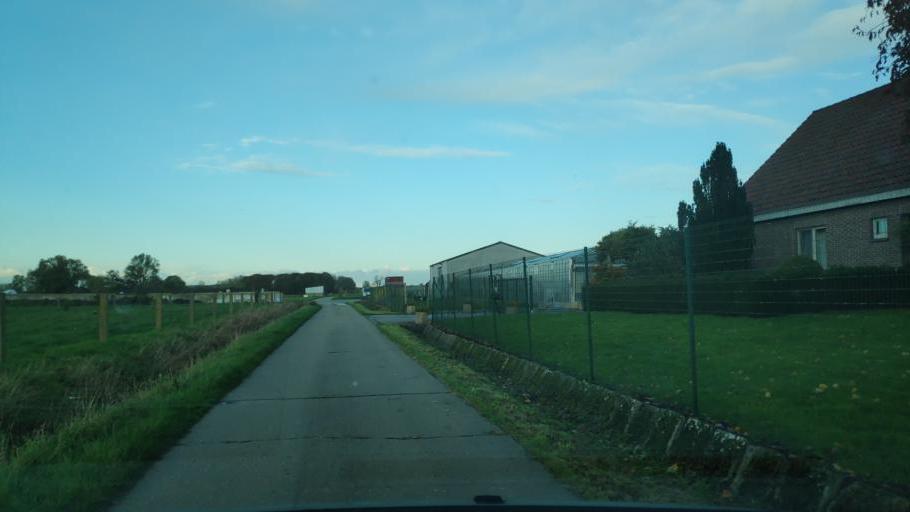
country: BE
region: Flanders
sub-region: Provincie Oost-Vlaanderen
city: Aalter
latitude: 51.0957
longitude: 3.4765
